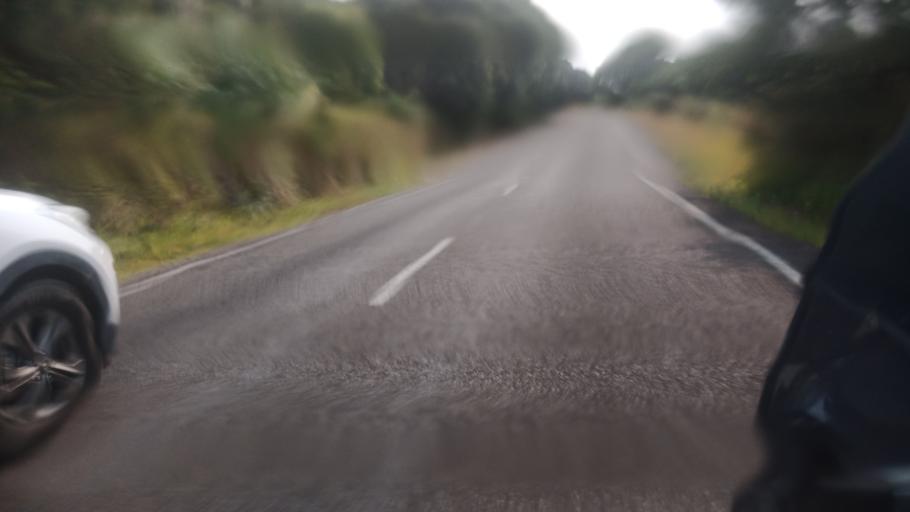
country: NZ
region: Bay of Plenty
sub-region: Opotiki District
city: Opotiki
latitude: -37.8021
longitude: 177.6564
